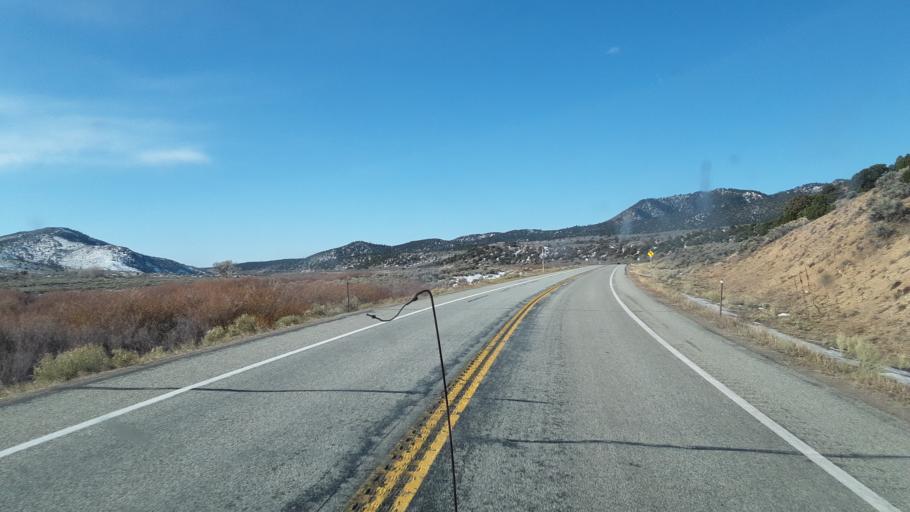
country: US
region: Colorado
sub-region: Costilla County
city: San Luis
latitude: 37.5152
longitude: -105.3043
